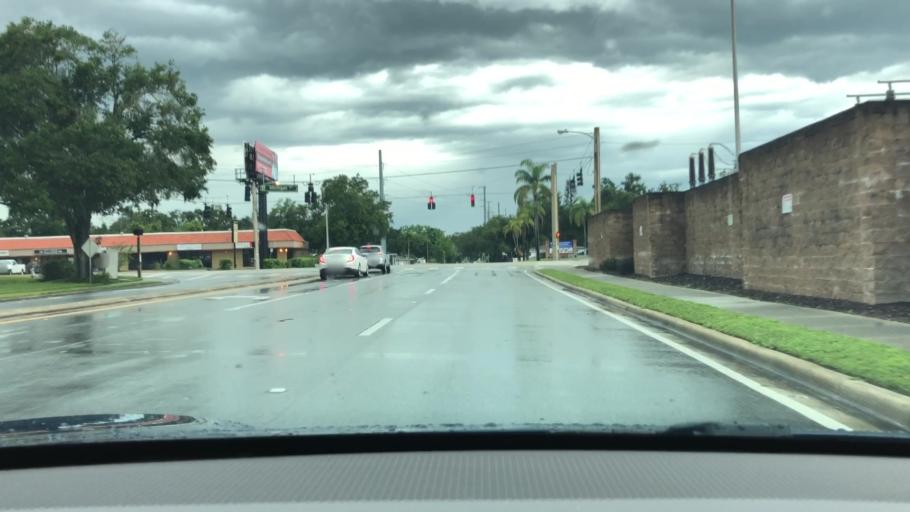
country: US
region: Florida
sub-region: Orange County
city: Conway
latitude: 28.5126
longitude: -81.3515
